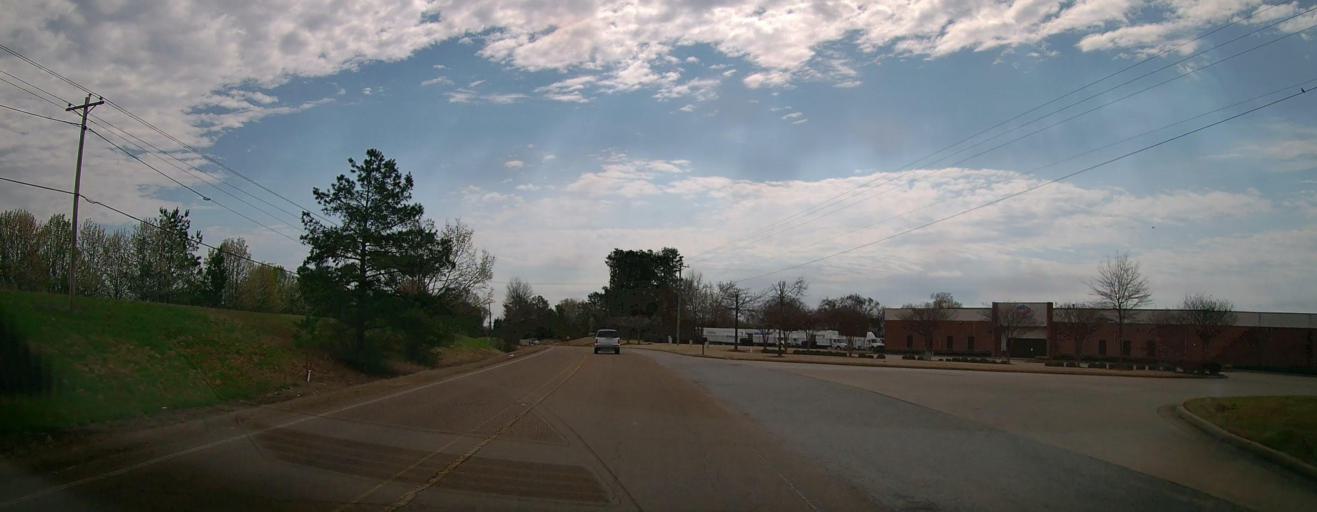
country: US
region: Mississippi
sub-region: De Soto County
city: Olive Branch
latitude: 34.9270
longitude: -89.7877
